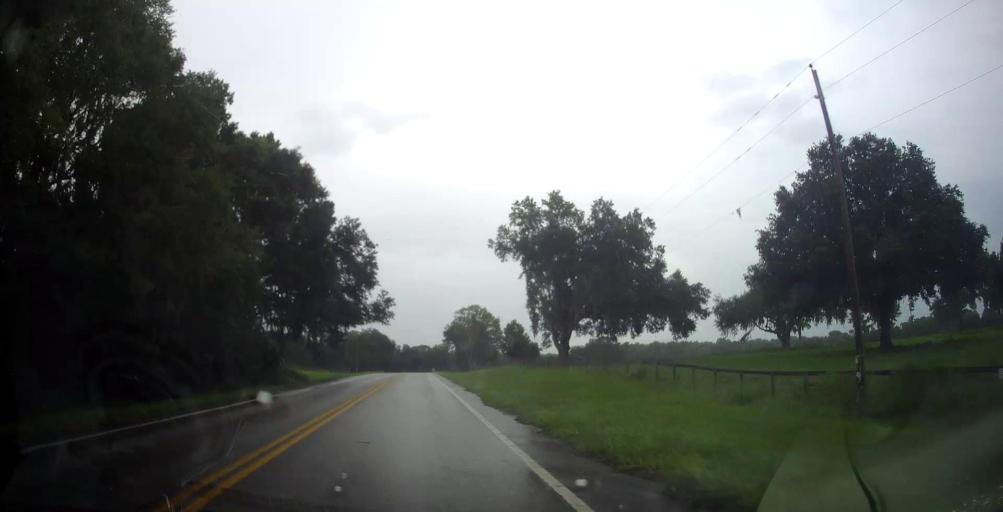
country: US
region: Florida
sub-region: Marion County
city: Citra
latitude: 29.4013
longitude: -82.2487
